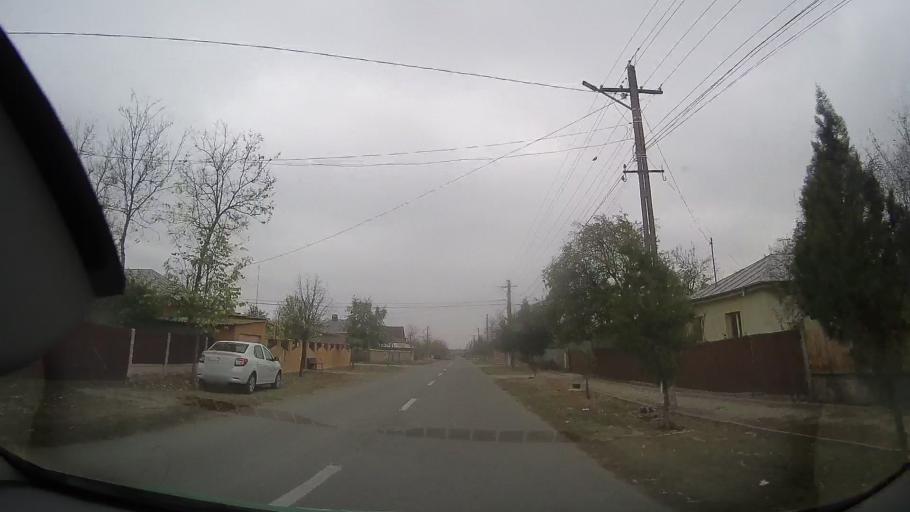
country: RO
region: Ialomita
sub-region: Comuna Grindu
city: Grindu
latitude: 44.7691
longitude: 26.9066
